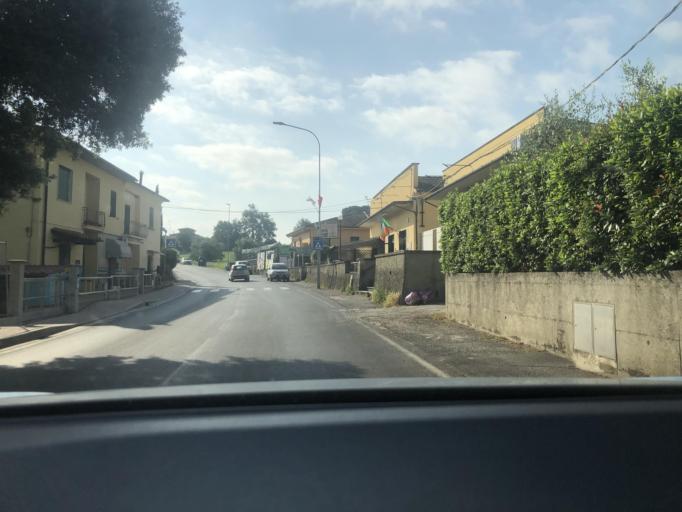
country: IT
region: Tuscany
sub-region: Provincia di Pistoia
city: Lamporecchio
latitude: 43.8069
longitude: 10.8668
